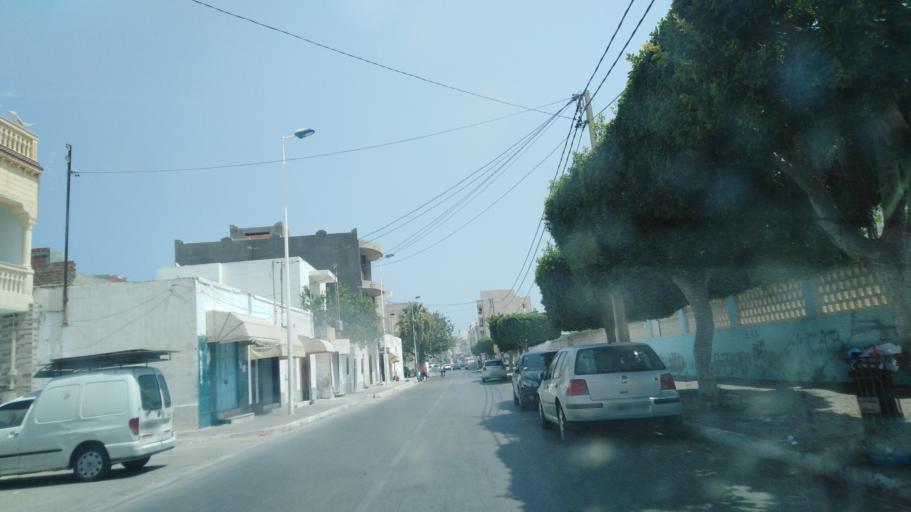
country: TN
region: Al Mahdiyah
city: Mahdia
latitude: 35.5106
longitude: 11.0497
